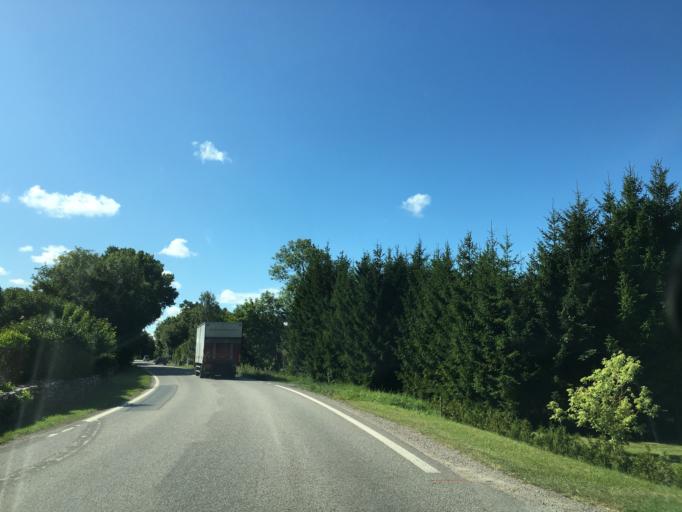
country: SE
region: Kalmar
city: Faerjestaden
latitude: 56.6381
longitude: 16.5160
